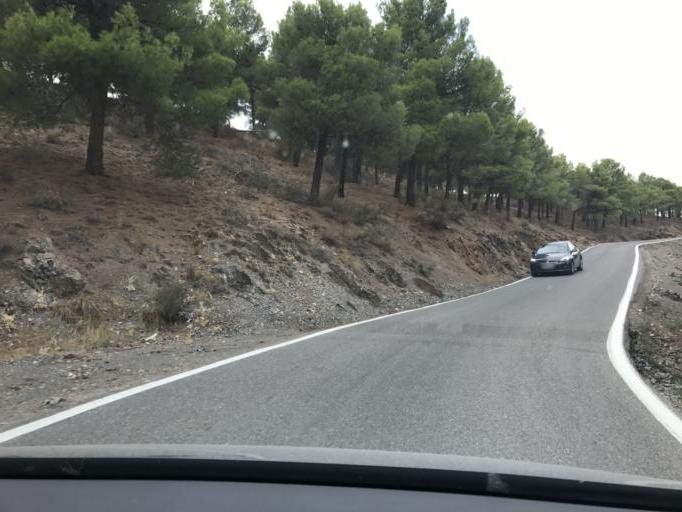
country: ES
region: Andalusia
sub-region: Provincia de Granada
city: Ferreira
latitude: 37.1699
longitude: -3.0501
